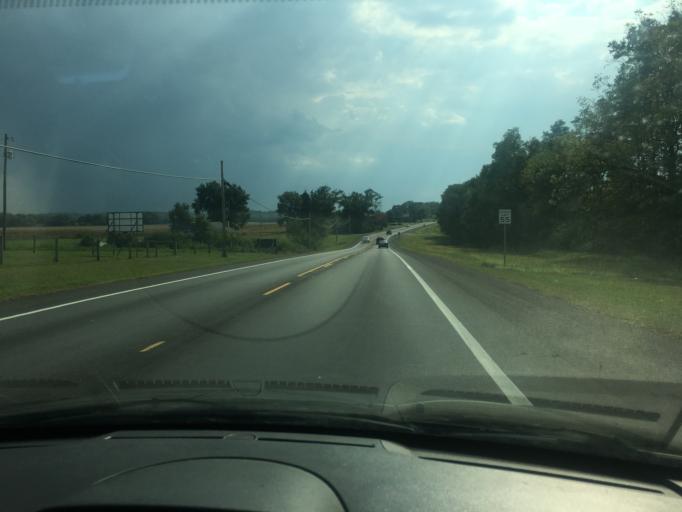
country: US
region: Ohio
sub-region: Champaign County
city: Urbana
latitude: 40.0779
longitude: -83.7642
